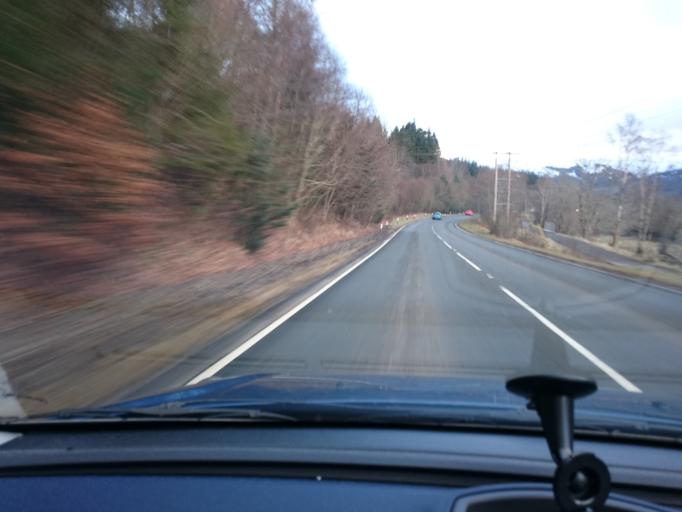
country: GB
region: Scotland
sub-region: Stirling
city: Callander
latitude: 56.3352
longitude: -4.3242
